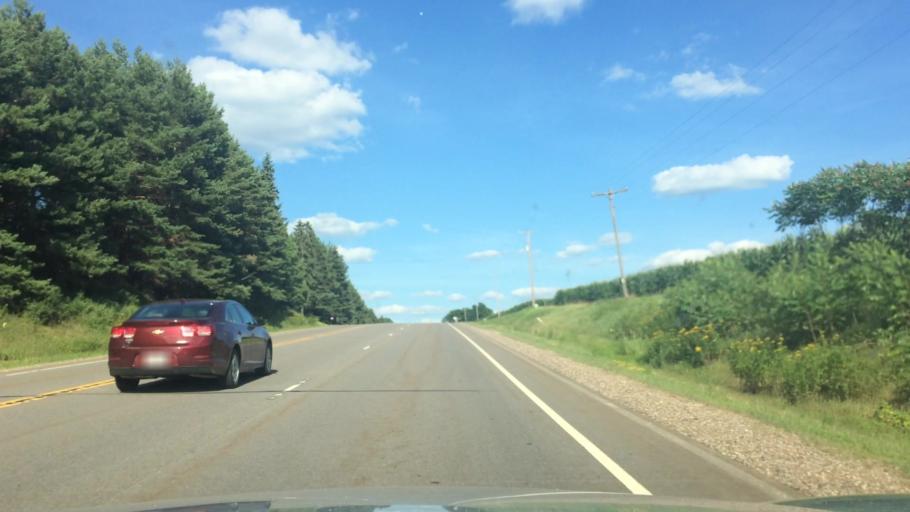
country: US
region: Wisconsin
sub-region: Lincoln County
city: Merrill
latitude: 45.1778
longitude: -89.6262
